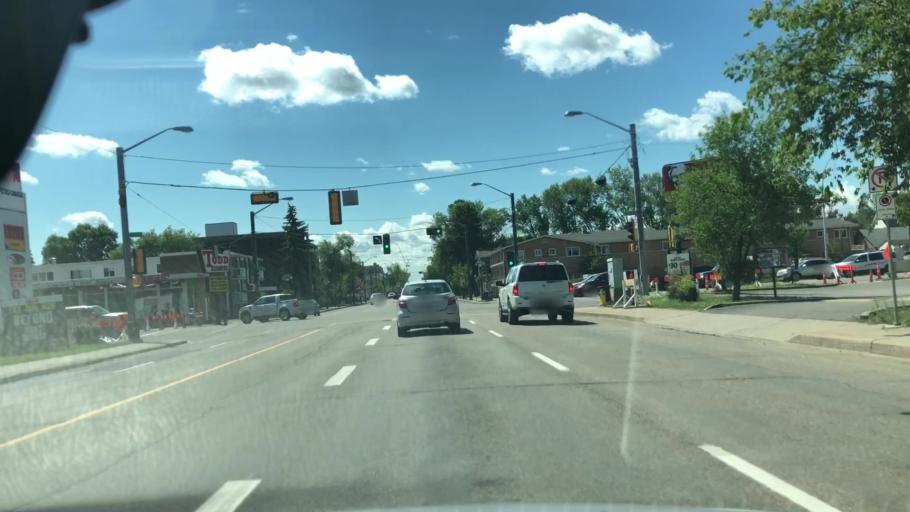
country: CA
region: Alberta
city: Edmonton
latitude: 53.5594
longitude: -113.5360
